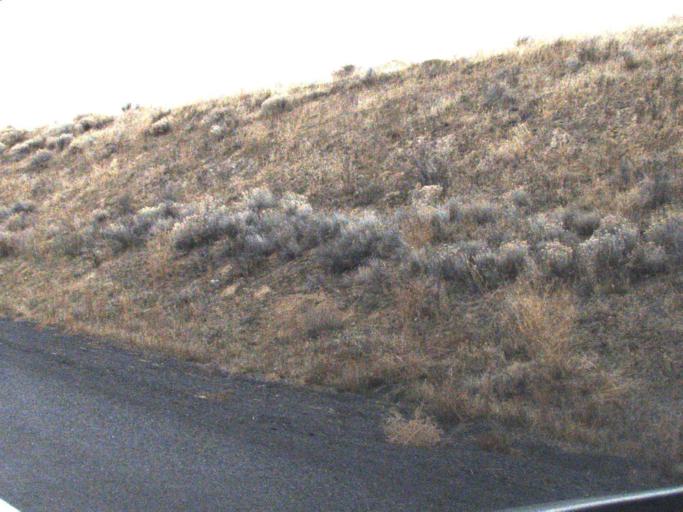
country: US
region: Washington
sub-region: Adams County
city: Ritzville
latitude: 46.7660
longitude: -118.3388
